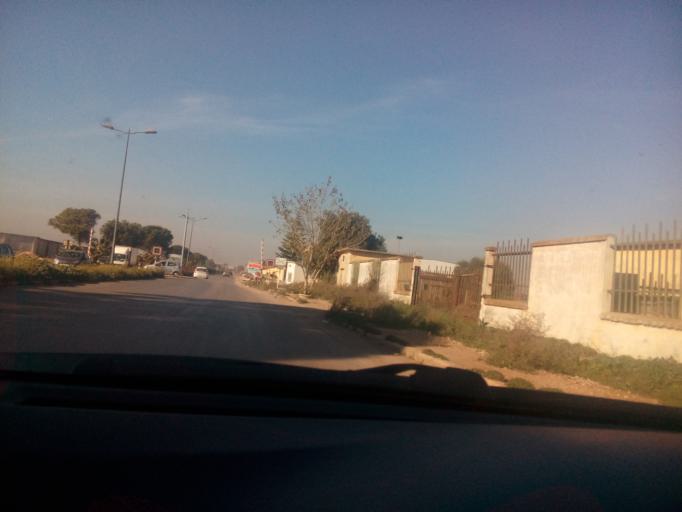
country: DZ
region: Oran
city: Es Senia
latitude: 35.6411
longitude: -0.6056
